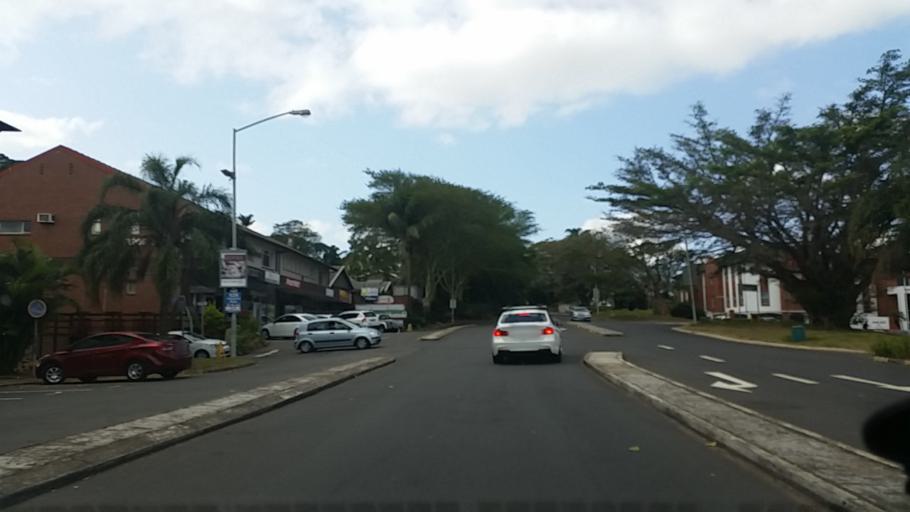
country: ZA
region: KwaZulu-Natal
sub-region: eThekwini Metropolitan Municipality
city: Berea
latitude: -29.8280
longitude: 30.9317
